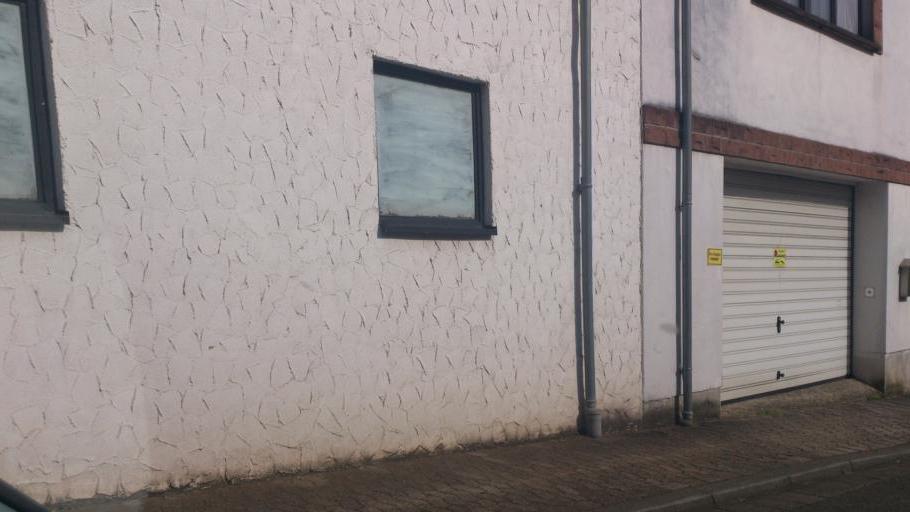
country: DE
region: Saarland
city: Bexbach
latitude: 49.3332
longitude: 7.2608
